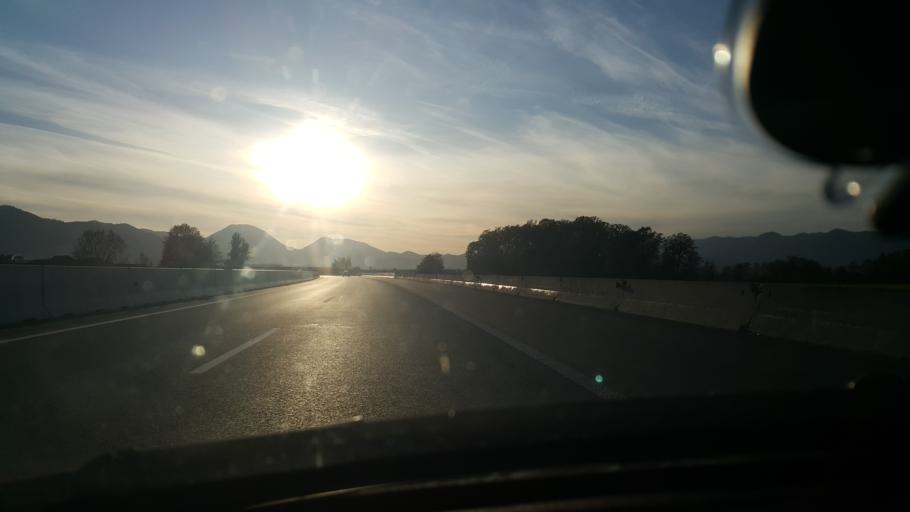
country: SI
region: Zalec
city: Sempeter v Savinj. Dolini
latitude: 46.2701
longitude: 15.1196
